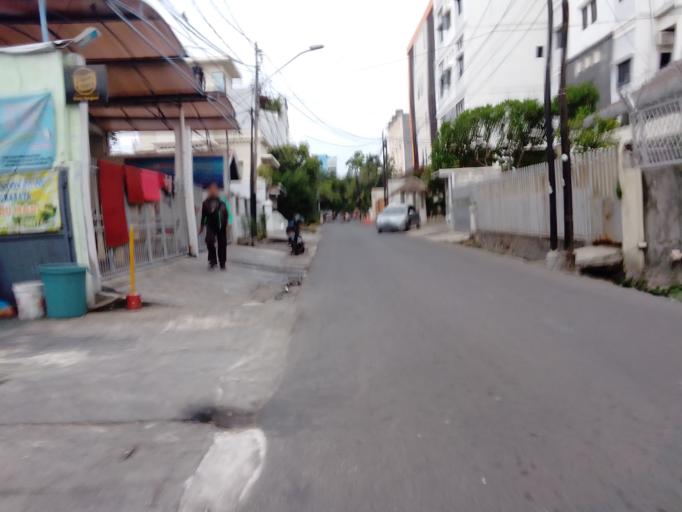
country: ID
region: Jakarta Raya
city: Jakarta
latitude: -6.1513
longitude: 106.8220
